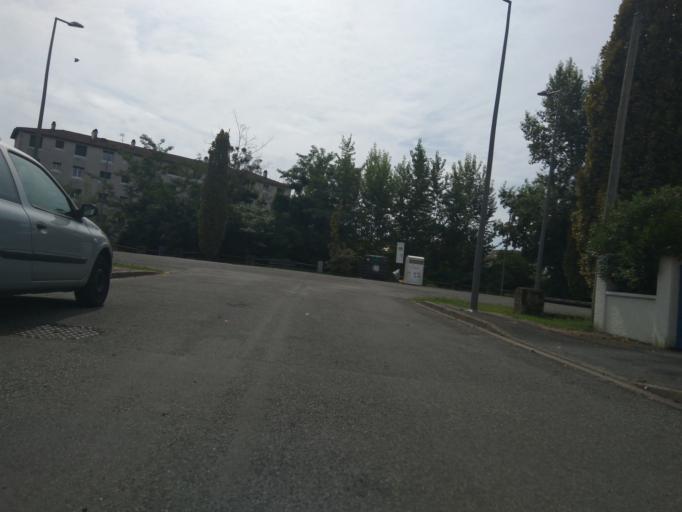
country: FR
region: Aquitaine
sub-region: Departement des Pyrenees-Atlantiques
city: Bizanos
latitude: 43.2922
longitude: -0.3549
